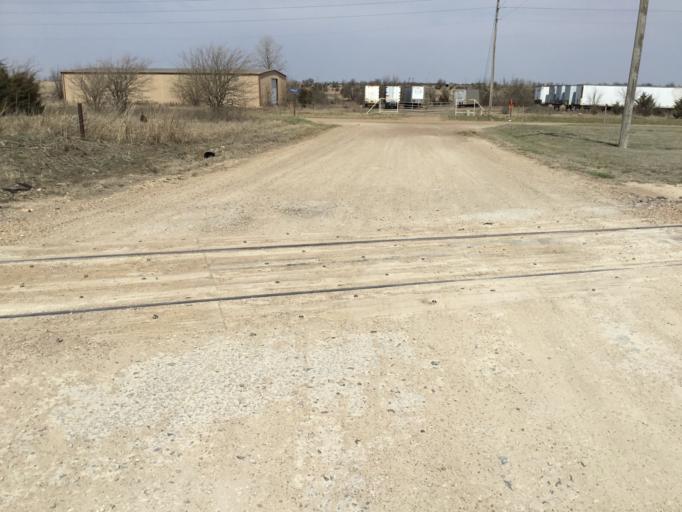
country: US
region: Kansas
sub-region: Butler County
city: El Dorado
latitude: 37.8242
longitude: -96.9125
